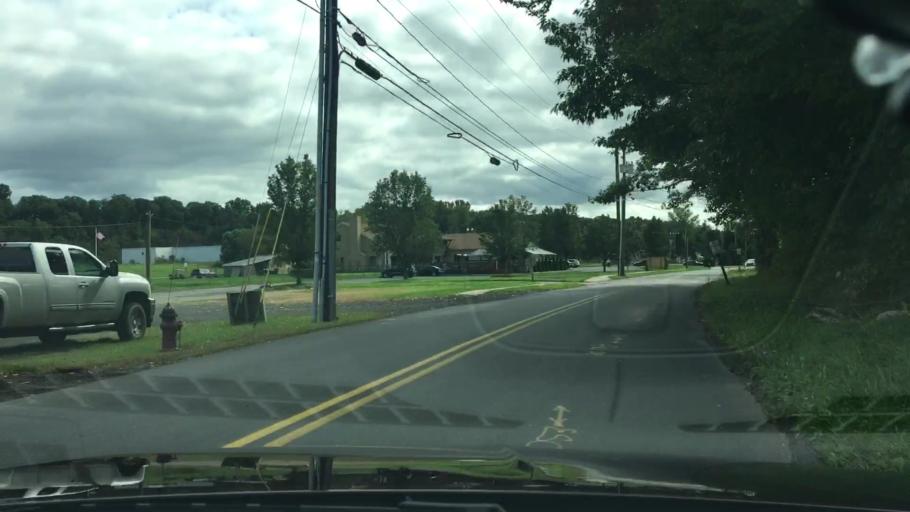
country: US
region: Connecticut
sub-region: Hartford County
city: Kensington
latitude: 41.6139
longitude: -72.7085
